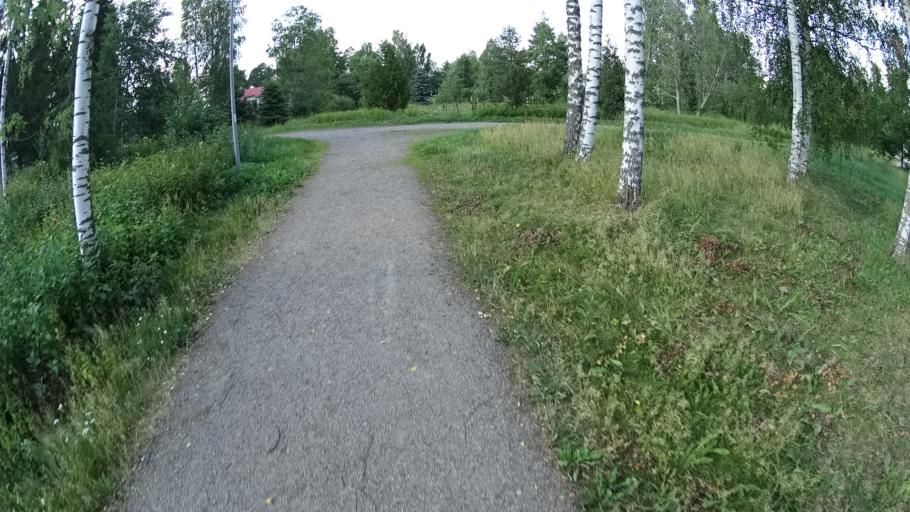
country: FI
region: Uusimaa
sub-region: Porvoo
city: Porvoo
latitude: 60.4071
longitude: 25.6627
